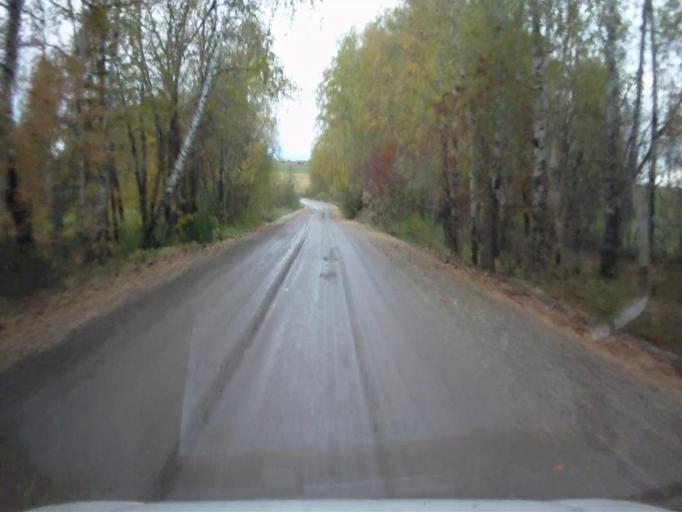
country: RU
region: Sverdlovsk
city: Mikhaylovsk
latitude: 56.1742
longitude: 59.2173
